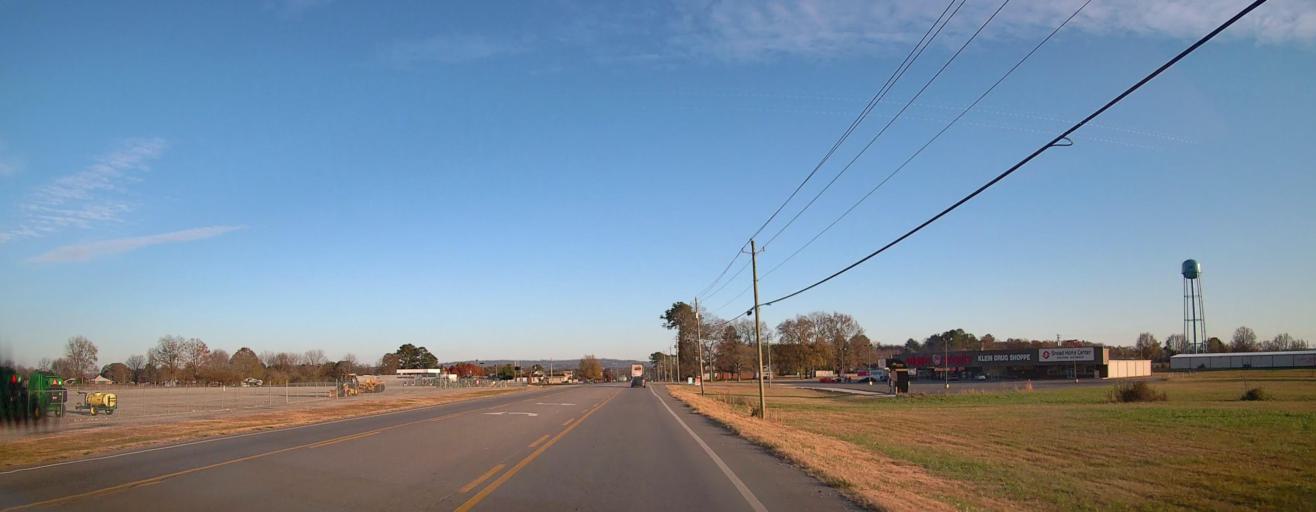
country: US
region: Alabama
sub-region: Blount County
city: Oneonta
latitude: 34.1183
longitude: -86.3932
